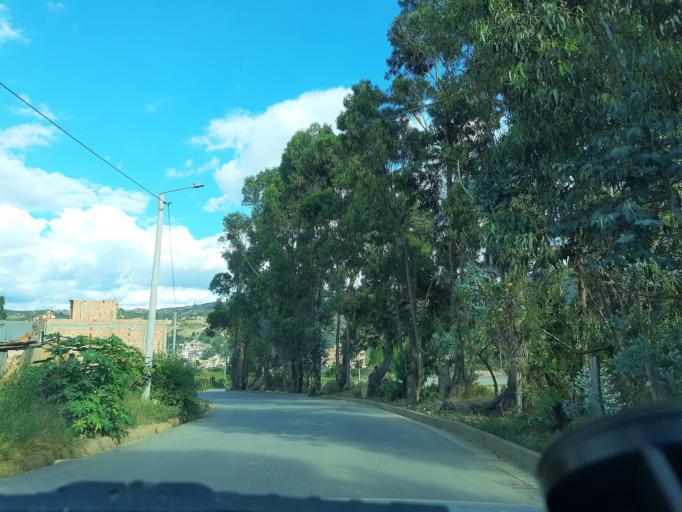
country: CO
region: Boyaca
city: Raquira
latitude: 5.5360
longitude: -73.6383
